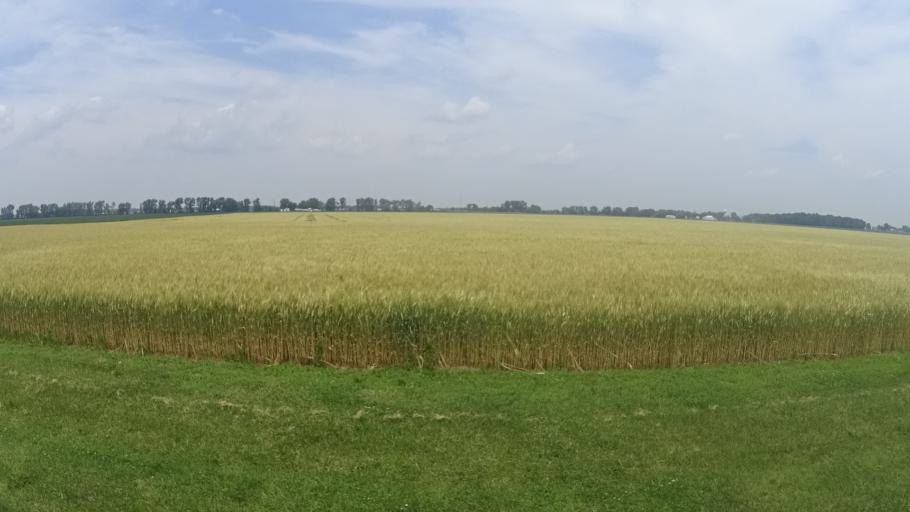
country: US
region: Ohio
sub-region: Erie County
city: Milan
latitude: 41.3118
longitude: -82.6489
